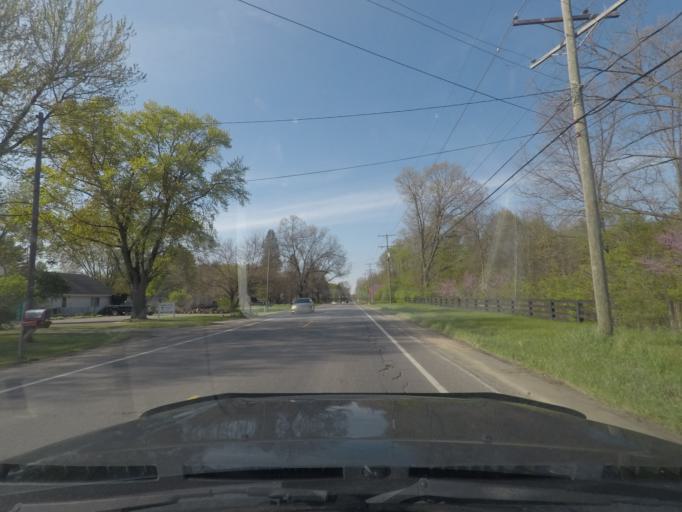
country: US
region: Michigan
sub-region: Berrien County
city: Niles
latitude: 41.7985
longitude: -86.2546
